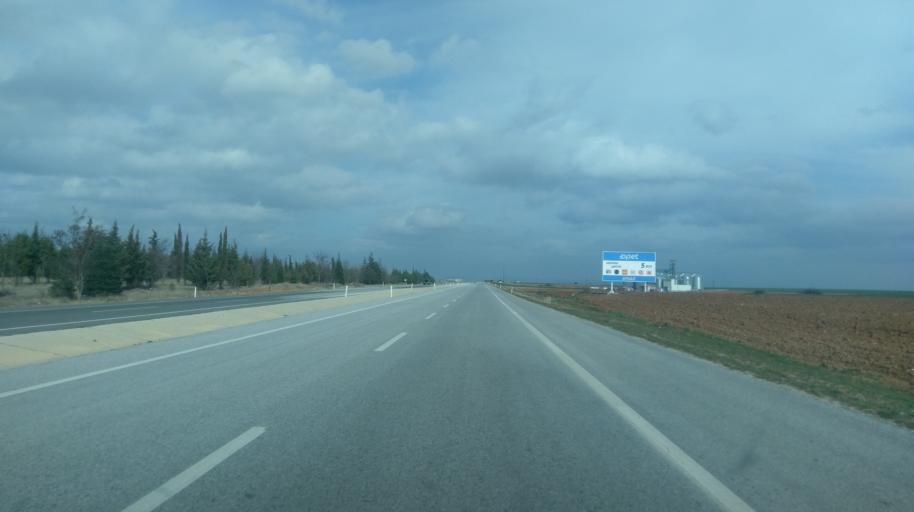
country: TR
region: Kirklareli
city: Kirklareli
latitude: 41.7001
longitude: 27.1567
